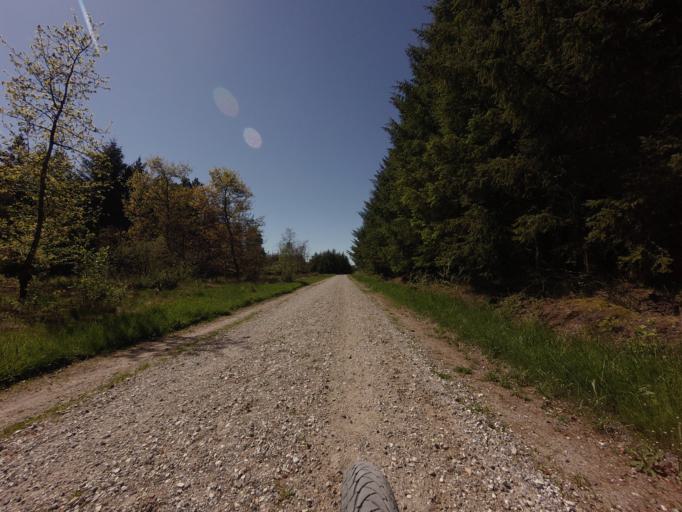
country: DK
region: North Denmark
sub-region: Jammerbugt Kommune
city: Pandrup
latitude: 57.2283
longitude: 9.5707
